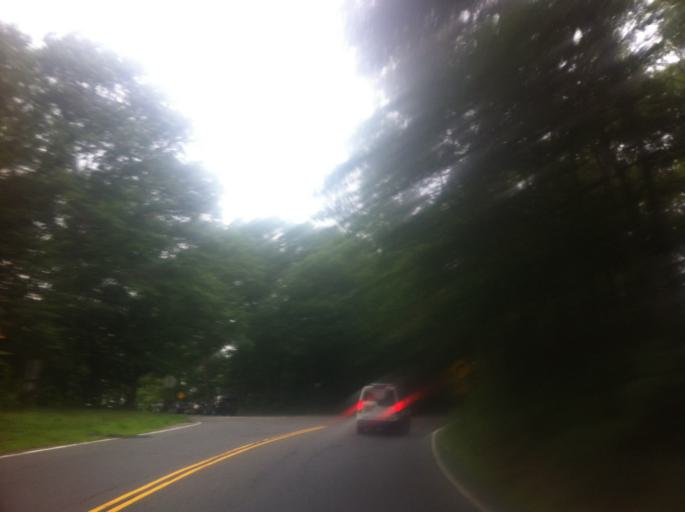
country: US
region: New York
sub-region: Nassau County
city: Bethpage
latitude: 40.7354
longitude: -73.4700
